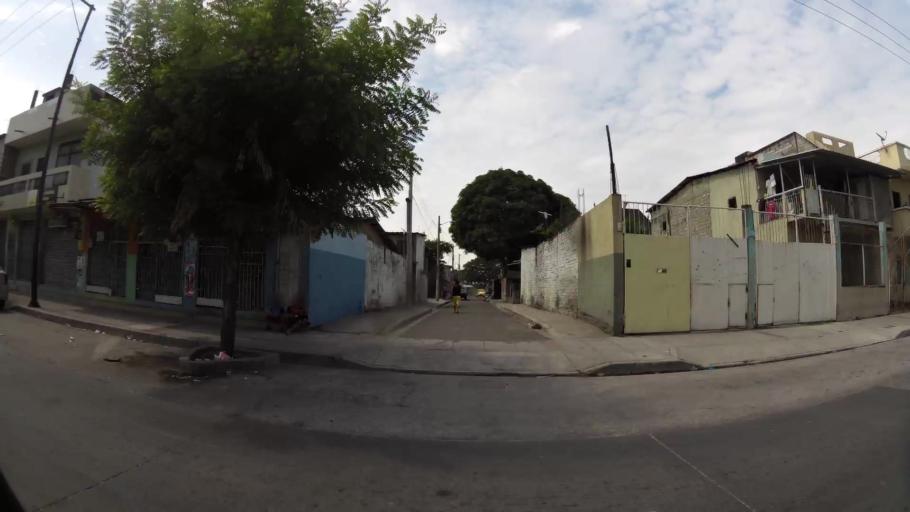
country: EC
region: Guayas
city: Guayaquil
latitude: -2.2818
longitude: -79.8829
